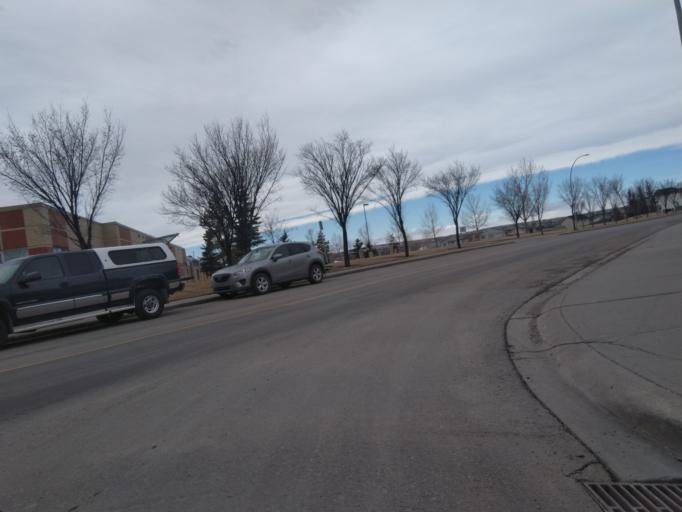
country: CA
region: Alberta
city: Calgary
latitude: 51.1651
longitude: -114.0455
